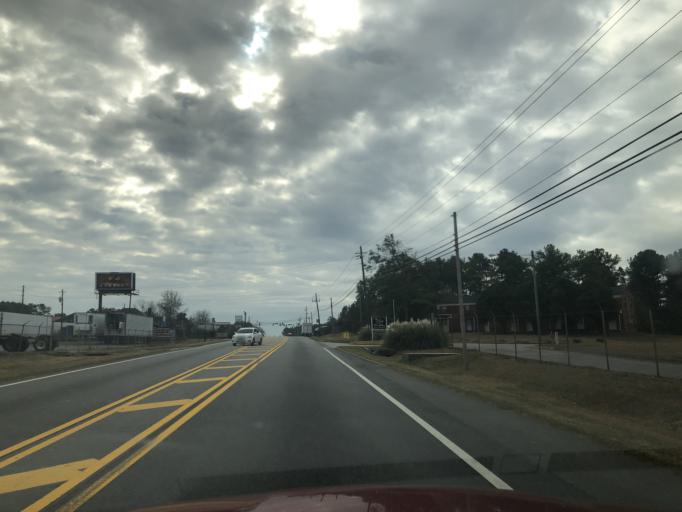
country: US
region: Georgia
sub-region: Clayton County
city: Conley
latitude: 33.6205
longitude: -84.3092
